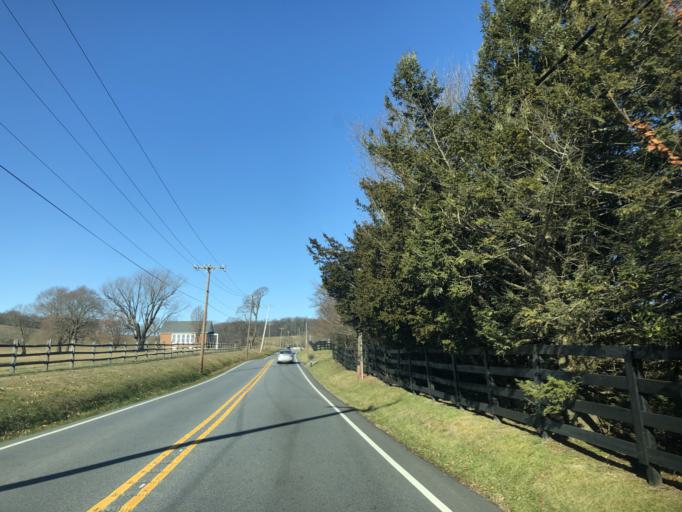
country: US
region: Pennsylvania
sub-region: Chester County
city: Upland
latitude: 39.9179
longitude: -75.8190
